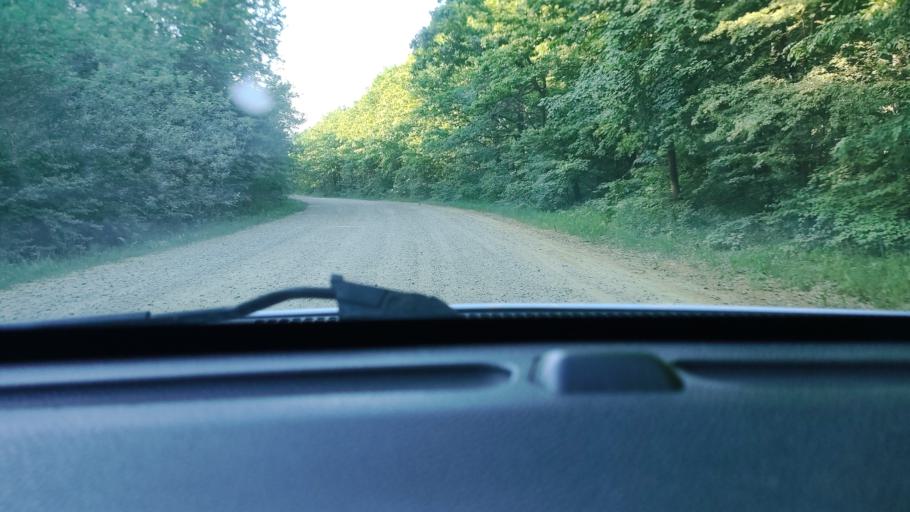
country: RU
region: Krasnodarskiy
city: Goryachiy Klyuch
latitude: 44.7094
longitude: 38.9924
